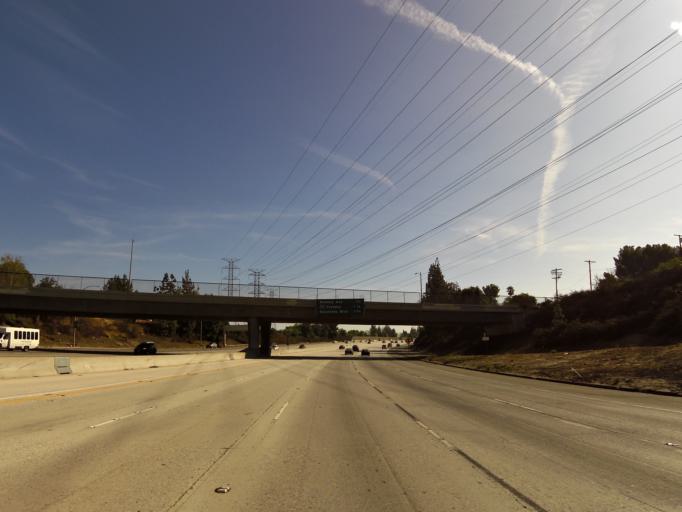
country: US
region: California
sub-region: Los Angeles County
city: San Fernando
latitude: 34.2775
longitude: -118.4988
